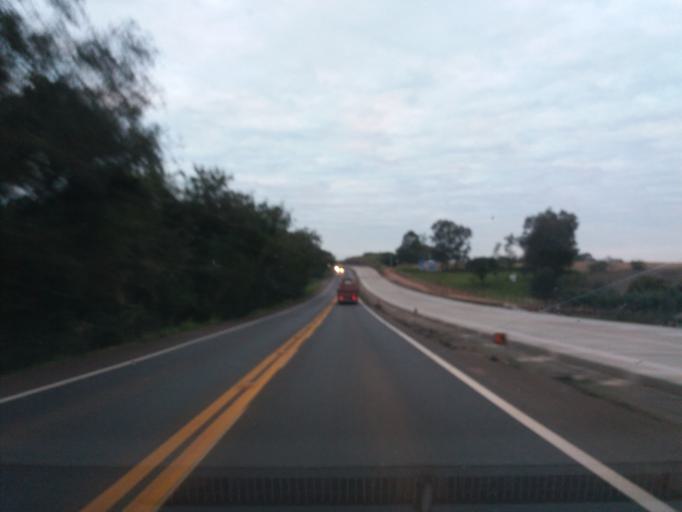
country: BR
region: Parana
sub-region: Realeza
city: Realeza
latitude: -25.3963
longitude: -53.5766
